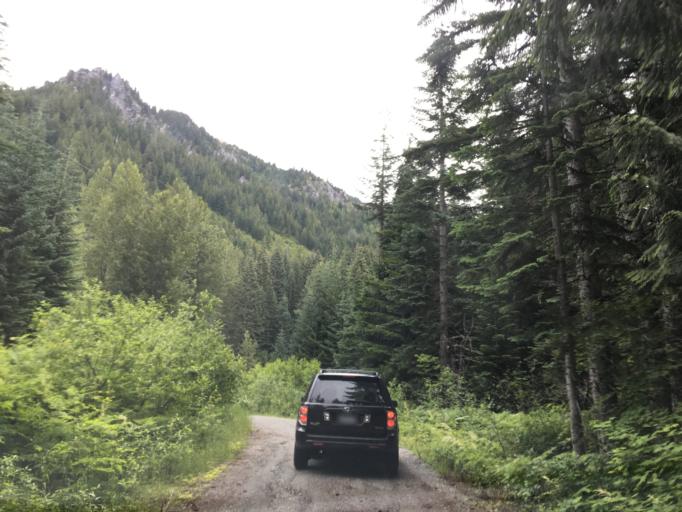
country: US
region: Washington
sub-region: Chelan County
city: Leavenworth
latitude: 47.7484
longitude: -121.1242
